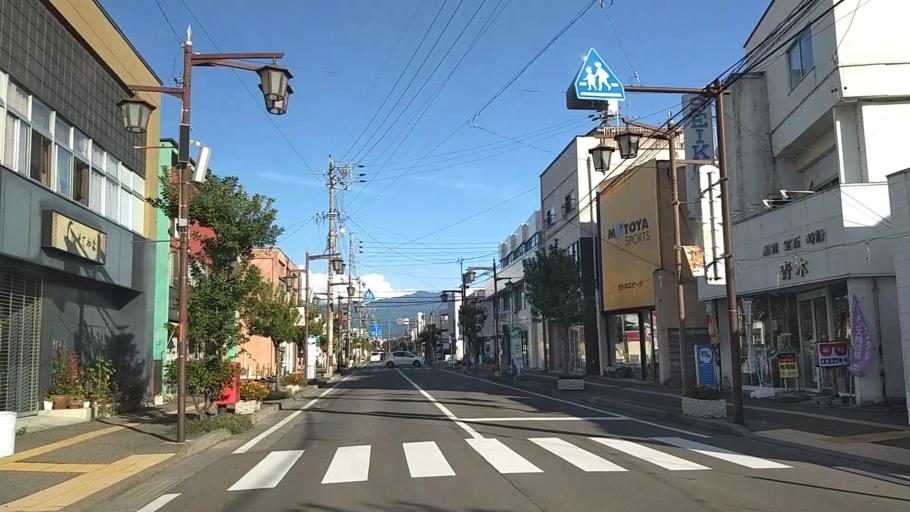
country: JP
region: Nagano
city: Nagano-shi
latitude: 36.5772
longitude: 138.1421
